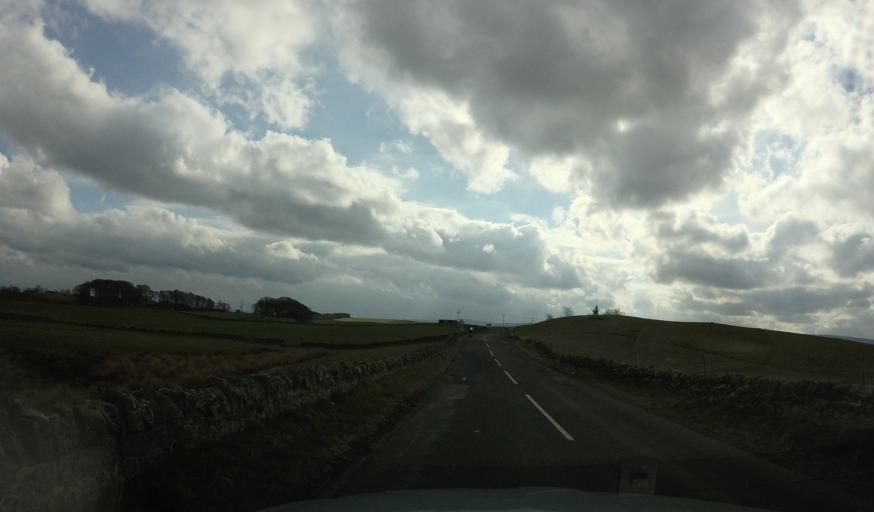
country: GB
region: Scotland
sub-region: Midlothian
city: Penicuik
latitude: 55.7994
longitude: -3.1582
